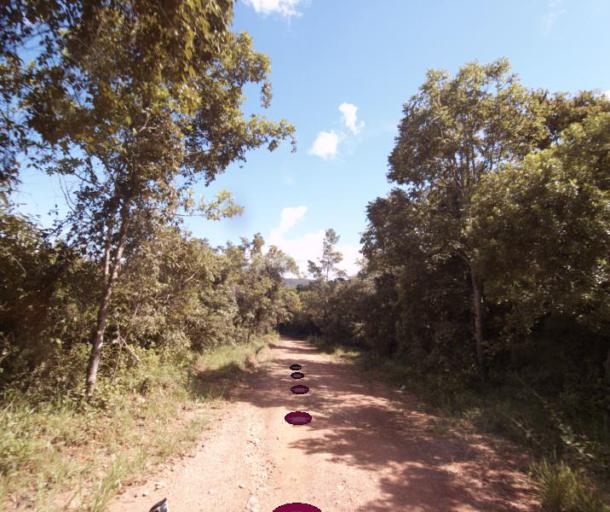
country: BR
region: Goias
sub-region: Pirenopolis
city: Pirenopolis
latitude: -15.7786
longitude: -48.9412
